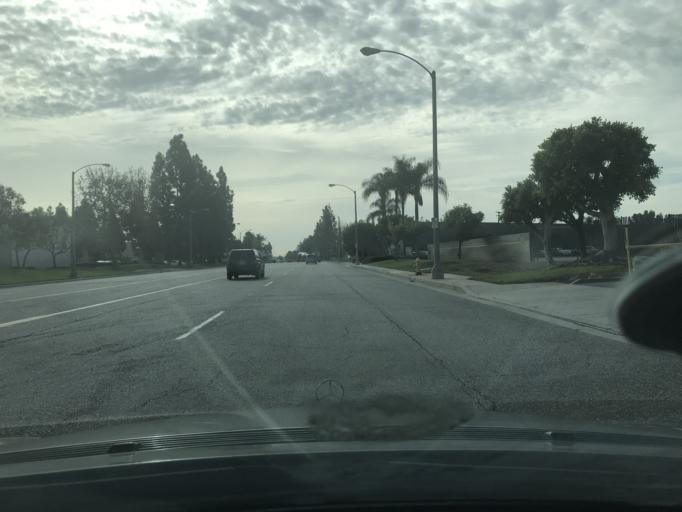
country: US
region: California
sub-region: Los Angeles County
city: Santa Fe Springs
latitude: 33.9561
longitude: -118.0718
